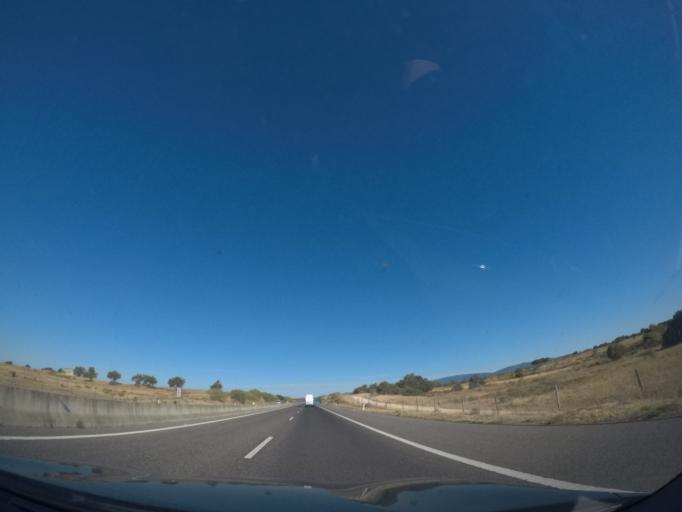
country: PT
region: Faro
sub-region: Lagoa
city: Lagoa
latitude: 37.1533
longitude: -8.4584
